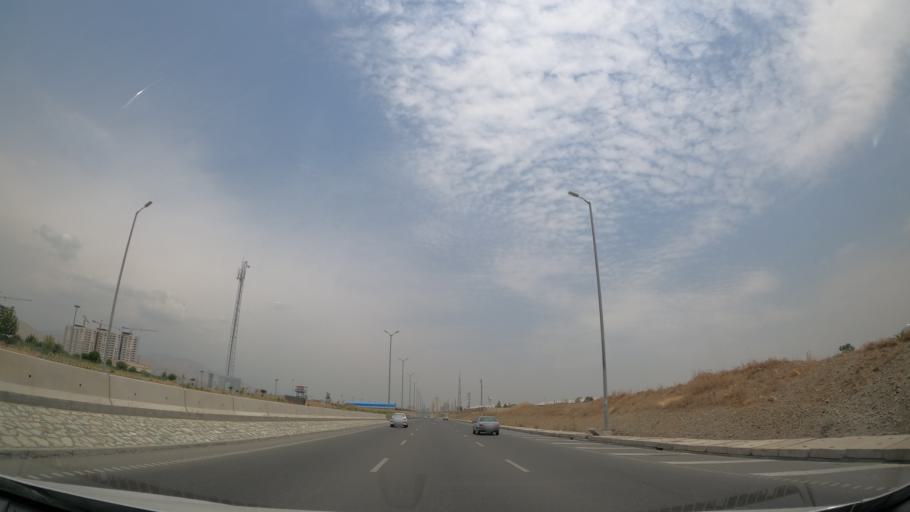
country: IR
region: Tehran
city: Shahr-e Qods
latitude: 35.7390
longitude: 51.2225
